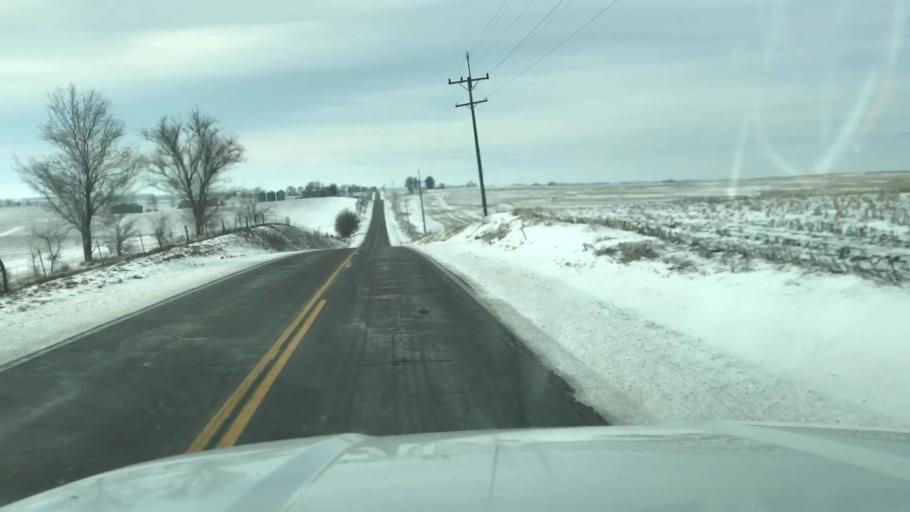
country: US
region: Missouri
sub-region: Holt County
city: Oregon
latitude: 40.0702
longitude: -95.1355
